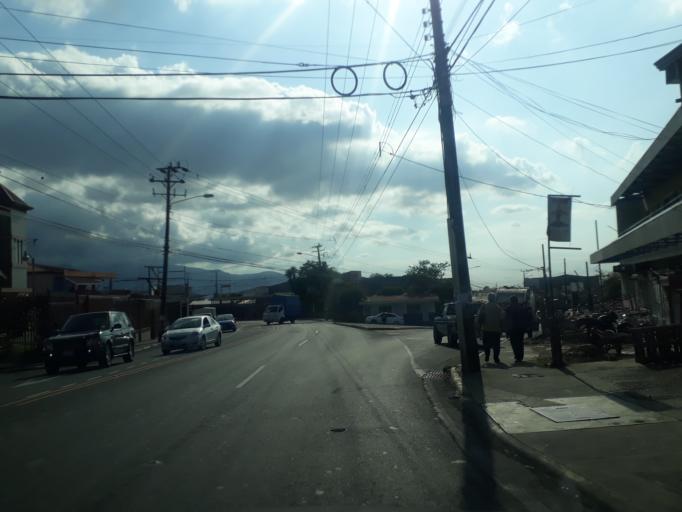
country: CR
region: San Jose
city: Purral
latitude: 9.9662
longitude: -84.0375
